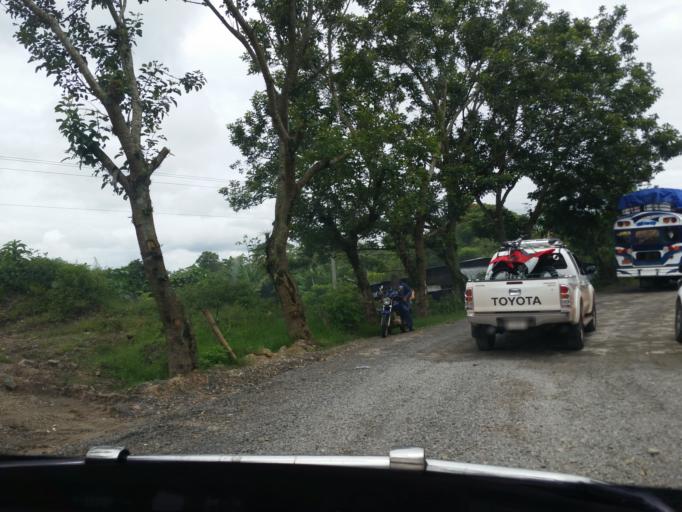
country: NI
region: Jinotega
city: Jinotega
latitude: 13.1768
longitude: -85.9175
